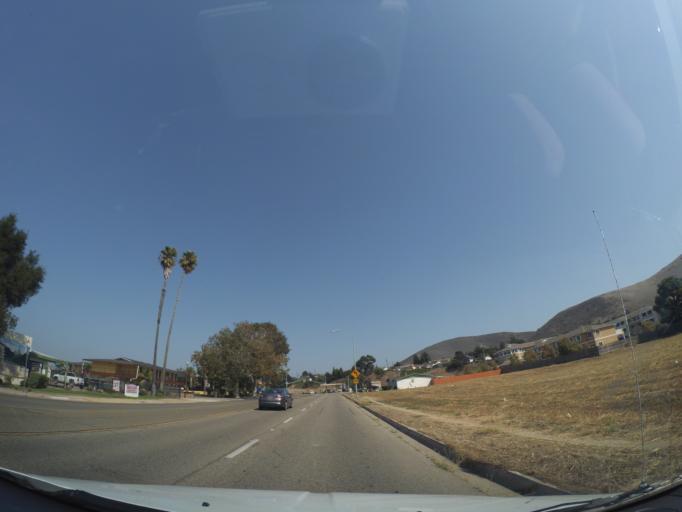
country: US
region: California
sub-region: Santa Barbara County
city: Lompoc
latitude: 34.6388
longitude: -120.4420
